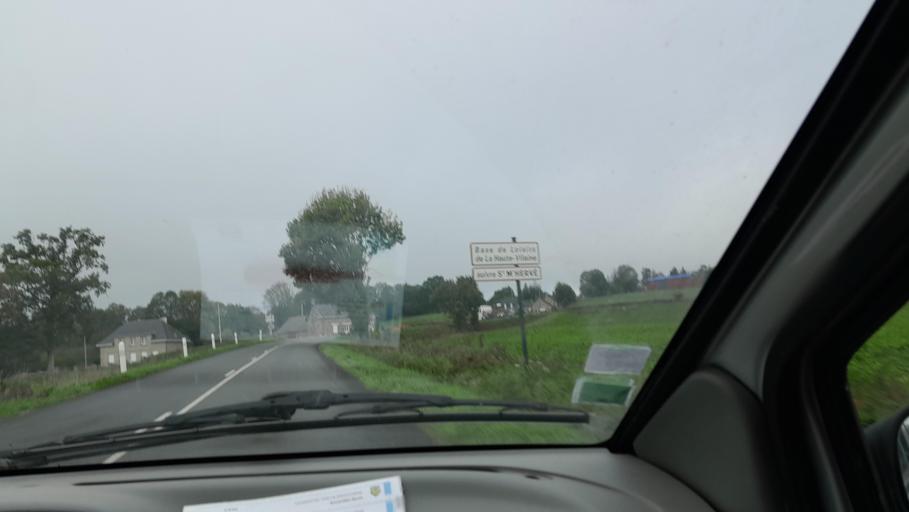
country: FR
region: Pays de la Loire
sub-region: Departement de la Mayenne
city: Juvigne
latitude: 48.2017
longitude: -1.0514
